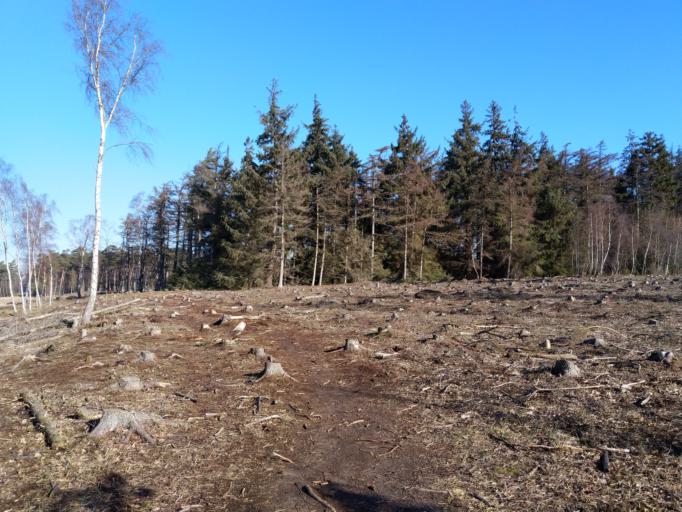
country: DK
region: Zealand
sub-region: Guldborgsund Kommune
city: Nykobing Falster
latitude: 54.6396
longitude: 11.9573
